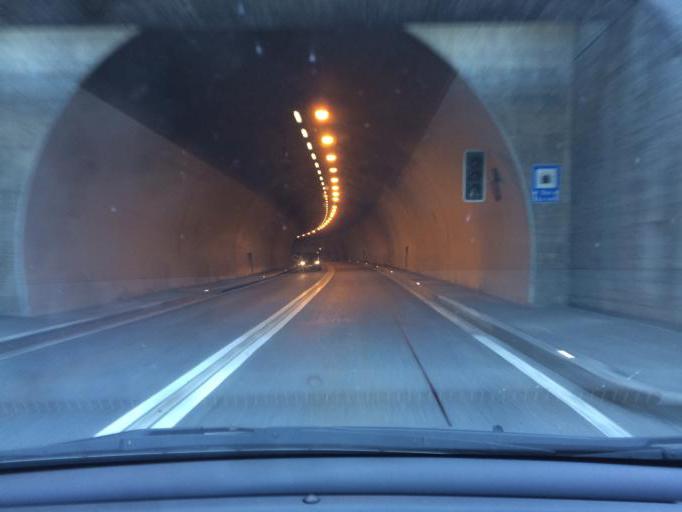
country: CH
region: Grisons
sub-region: Imboden District
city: Bonaduz
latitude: 46.8330
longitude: 9.3450
